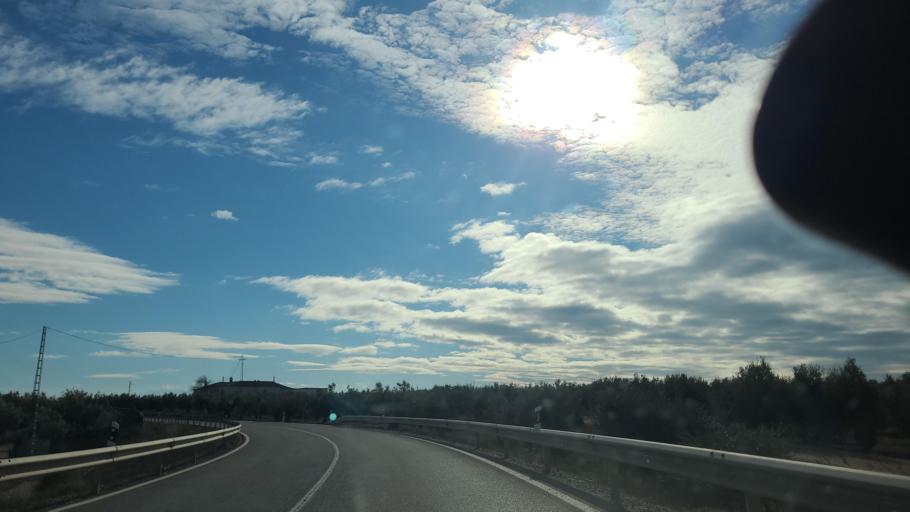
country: ES
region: Andalusia
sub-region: Provincia de Jaen
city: Espeluy
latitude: 38.0284
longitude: -3.8636
